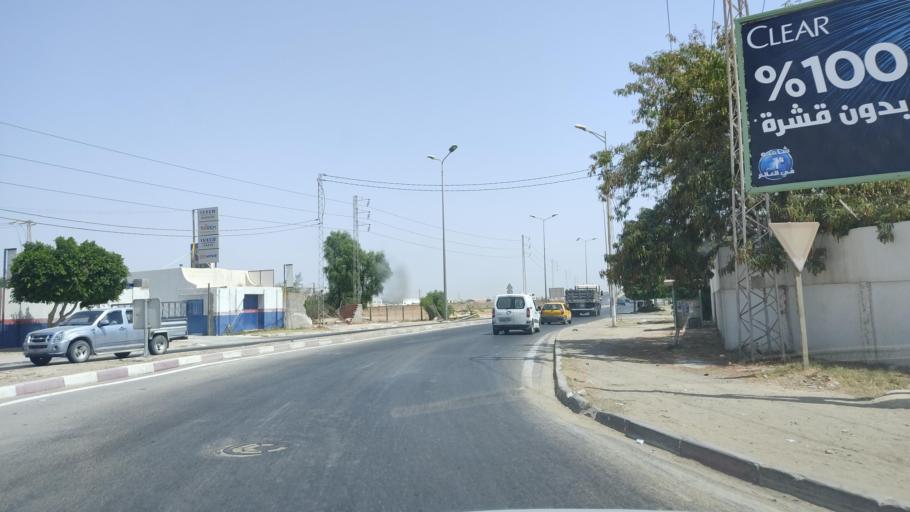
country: TN
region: Safaqis
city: Sfax
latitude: 34.6996
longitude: 10.7186
